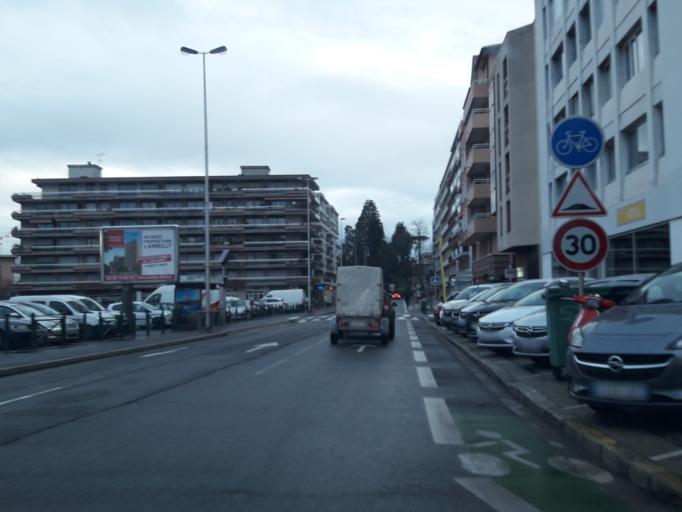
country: FR
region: Rhone-Alpes
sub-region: Departement de la Haute-Savoie
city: Annemasse
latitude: 46.1916
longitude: 6.2337
